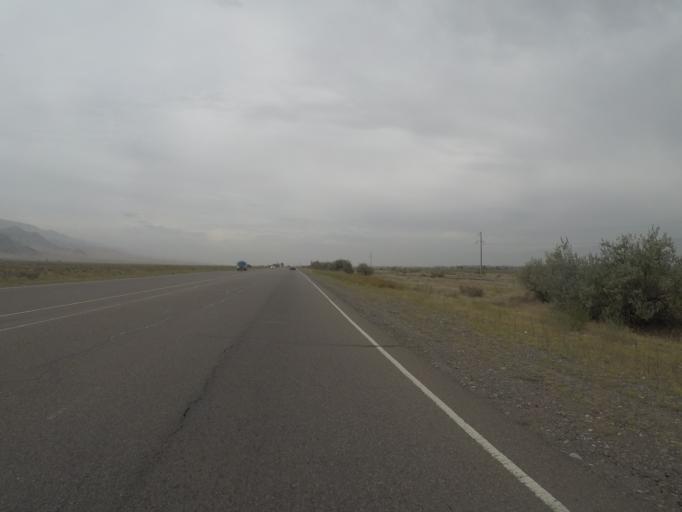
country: KG
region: Chuy
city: Tokmok
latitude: 42.8299
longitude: 75.4666
